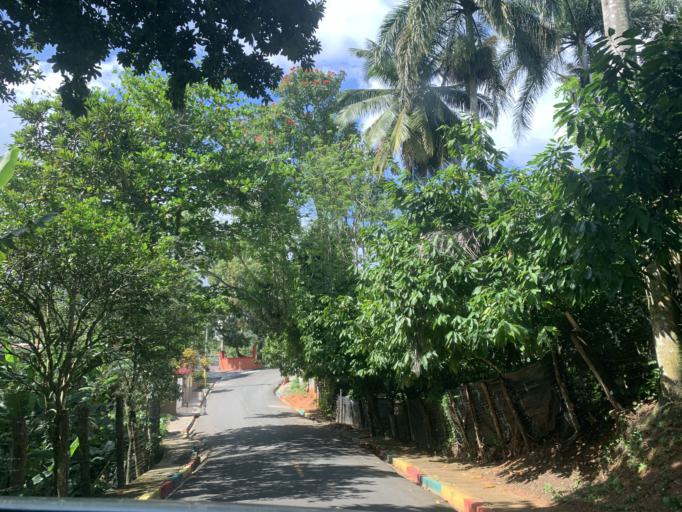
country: DO
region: Monte Plata
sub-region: Yamasa
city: Yamasa
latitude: 18.7686
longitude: -70.0255
